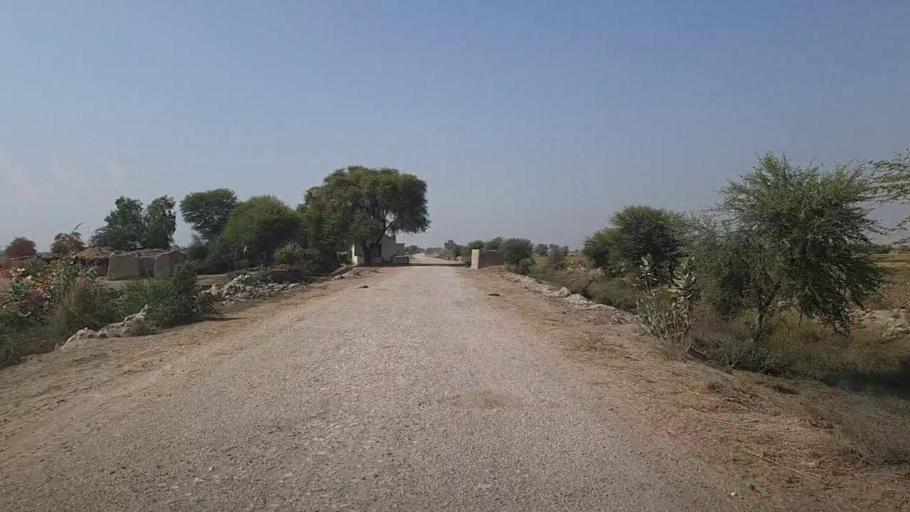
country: PK
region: Sindh
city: Kandhkot
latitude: 28.3907
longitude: 69.2862
